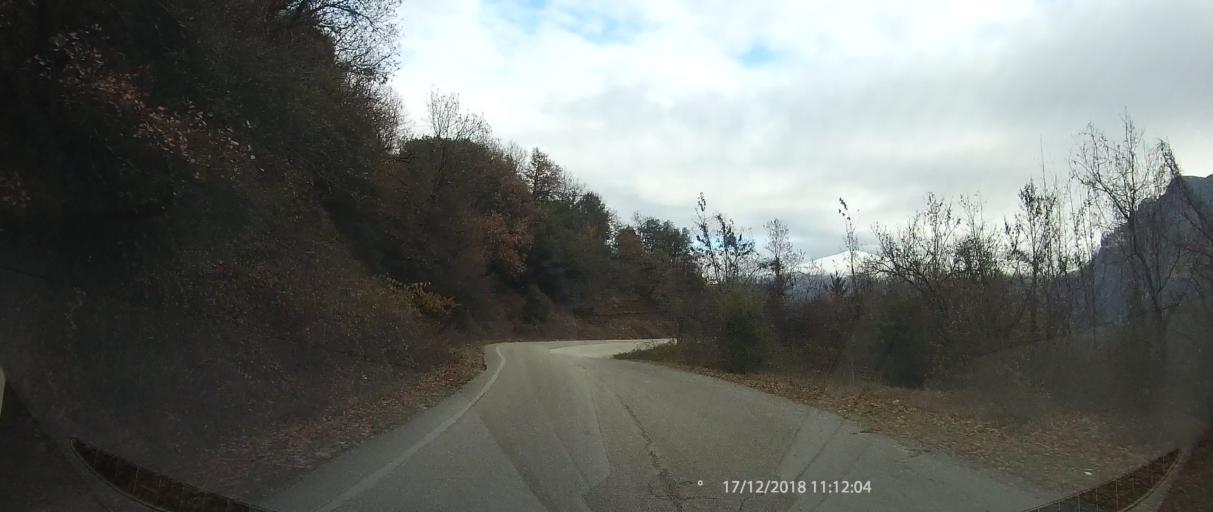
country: GR
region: Epirus
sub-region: Nomos Ioanninon
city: Kalpaki
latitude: 39.9413
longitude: 20.6773
